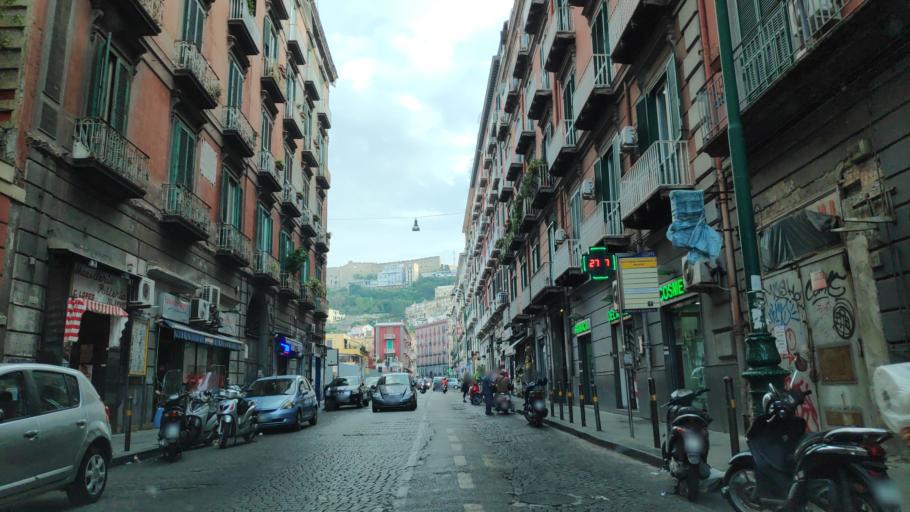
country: IT
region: Campania
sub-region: Provincia di Napoli
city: Napoli
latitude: 40.8510
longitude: 14.2422
